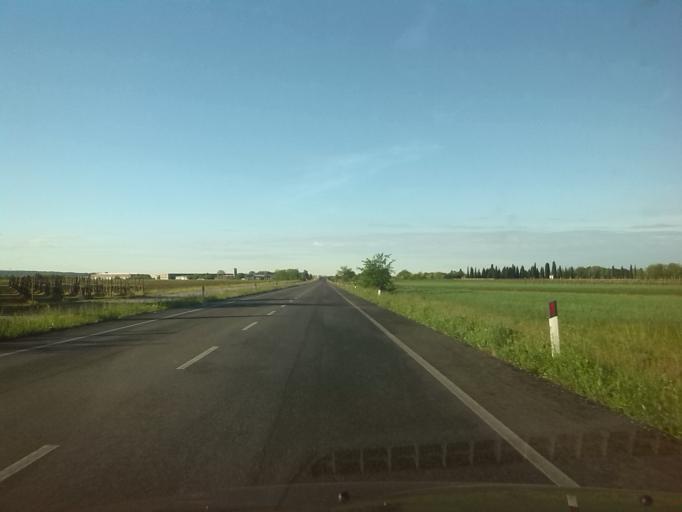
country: IT
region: Friuli Venezia Giulia
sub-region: Provincia di Gorizia
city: Mariano del Friuli
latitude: 45.9144
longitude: 13.4680
